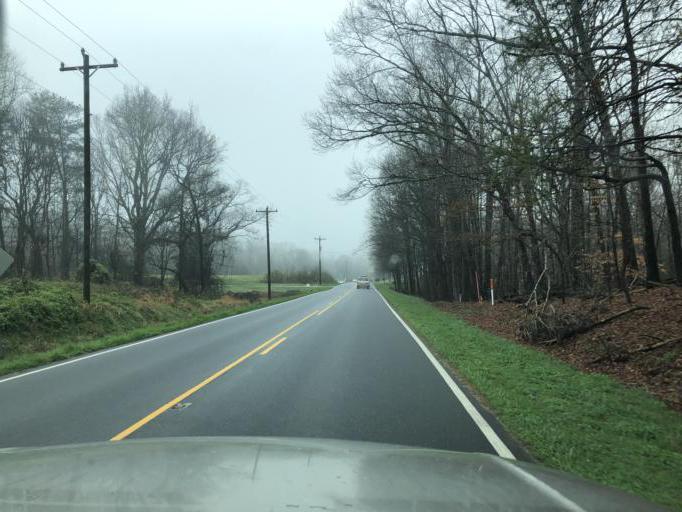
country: US
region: North Carolina
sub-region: Gaston County
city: Cherryville
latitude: 35.3713
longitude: -81.4087
